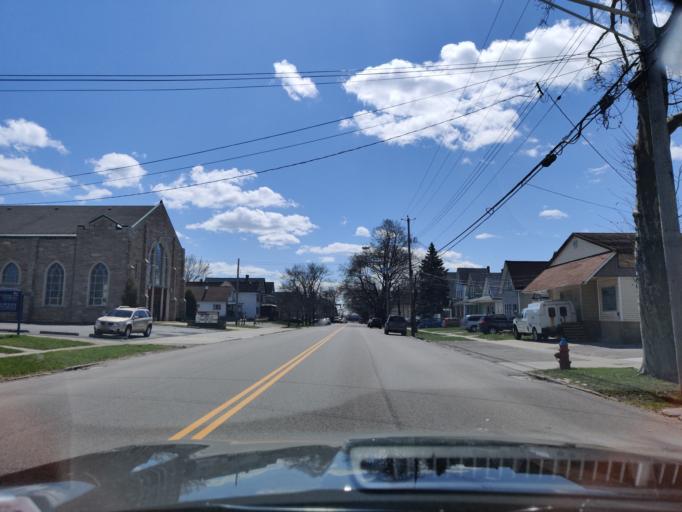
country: US
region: New York
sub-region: Erie County
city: Sloan
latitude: 42.8888
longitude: -78.8025
